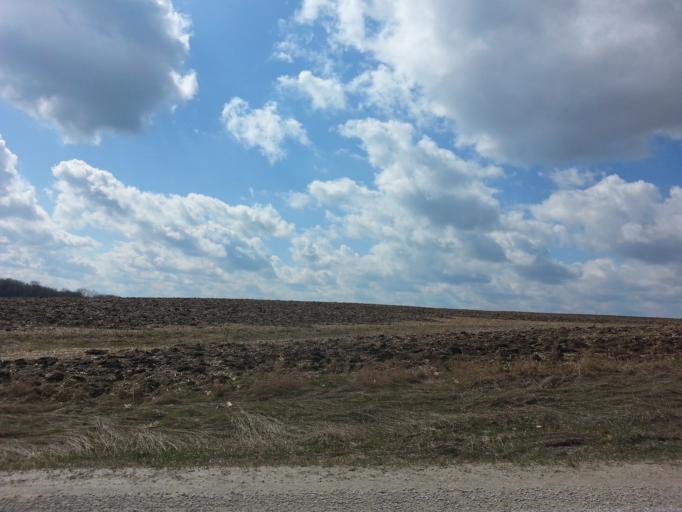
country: US
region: Minnesota
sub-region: Dodge County
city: Mantorville
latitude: 44.0781
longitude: -92.7184
